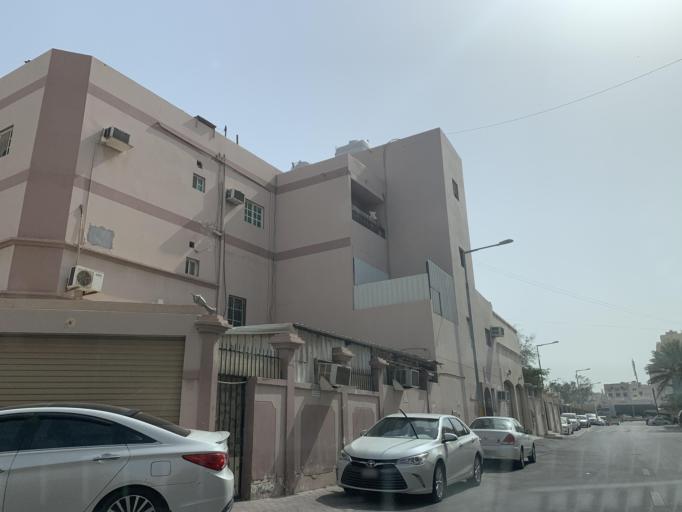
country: BH
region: Northern
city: Ar Rifa'
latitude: 26.1242
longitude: 50.5723
